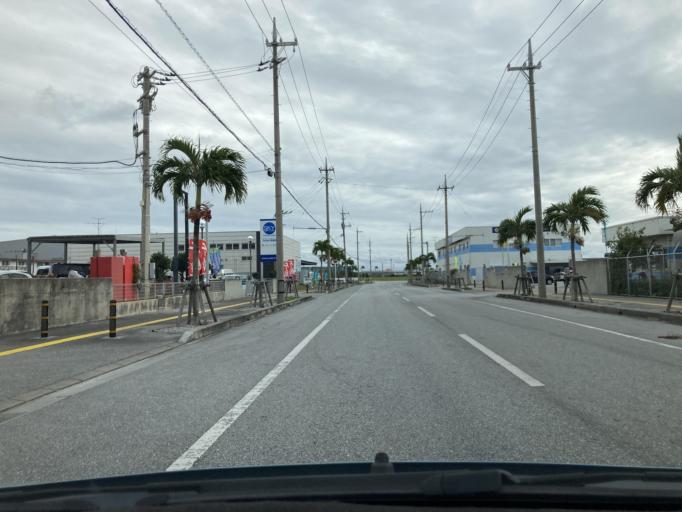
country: JP
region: Okinawa
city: Itoman
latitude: 26.1544
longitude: 127.6534
